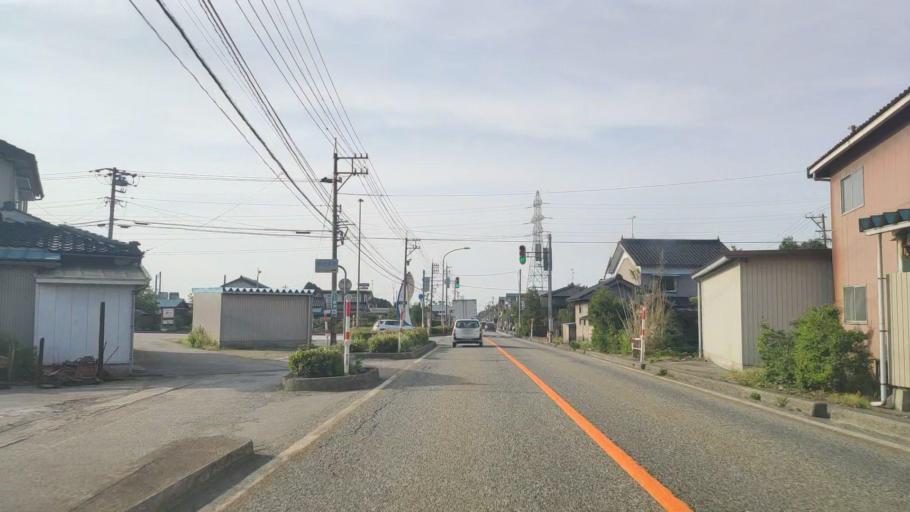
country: JP
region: Toyama
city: Yatsuomachi-higashikumisaka
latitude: 36.5674
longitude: 137.2107
